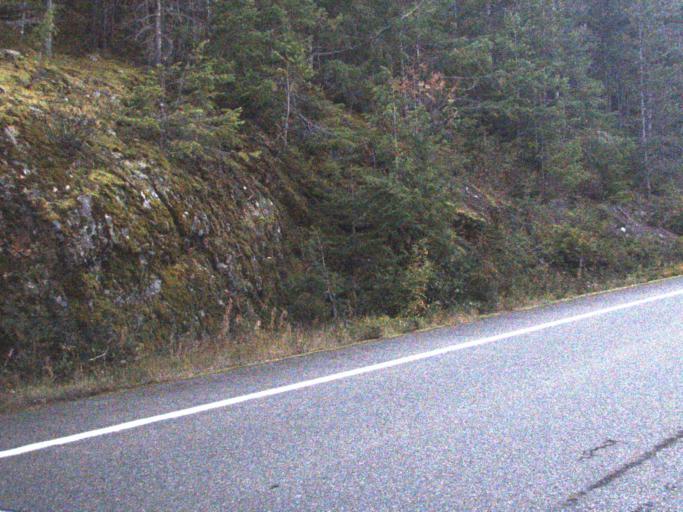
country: US
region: Washington
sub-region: Snohomish County
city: Darrington
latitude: 48.7254
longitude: -121.0323
